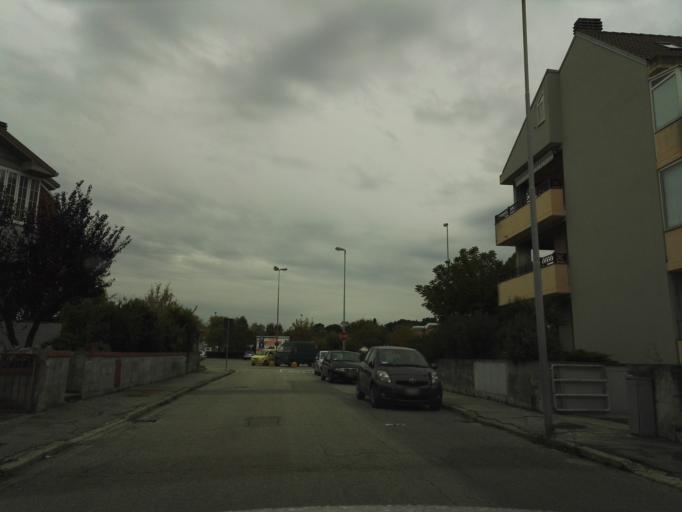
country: IT
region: The Marches
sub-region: Provincia di Pesaro e Urbino
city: Marotta
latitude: 43.7660
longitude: 13.1341
